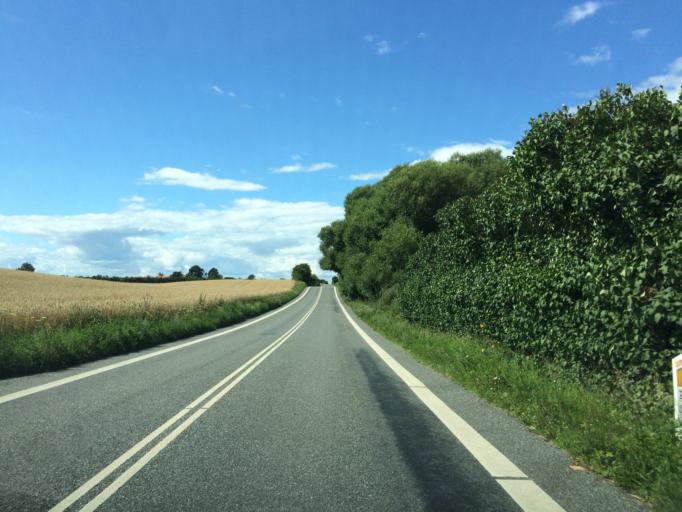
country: DK
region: South Denmark
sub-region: Faaborg-Midtfyn Kommune
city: Faaborg
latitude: 55.1367
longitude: 10.1903
